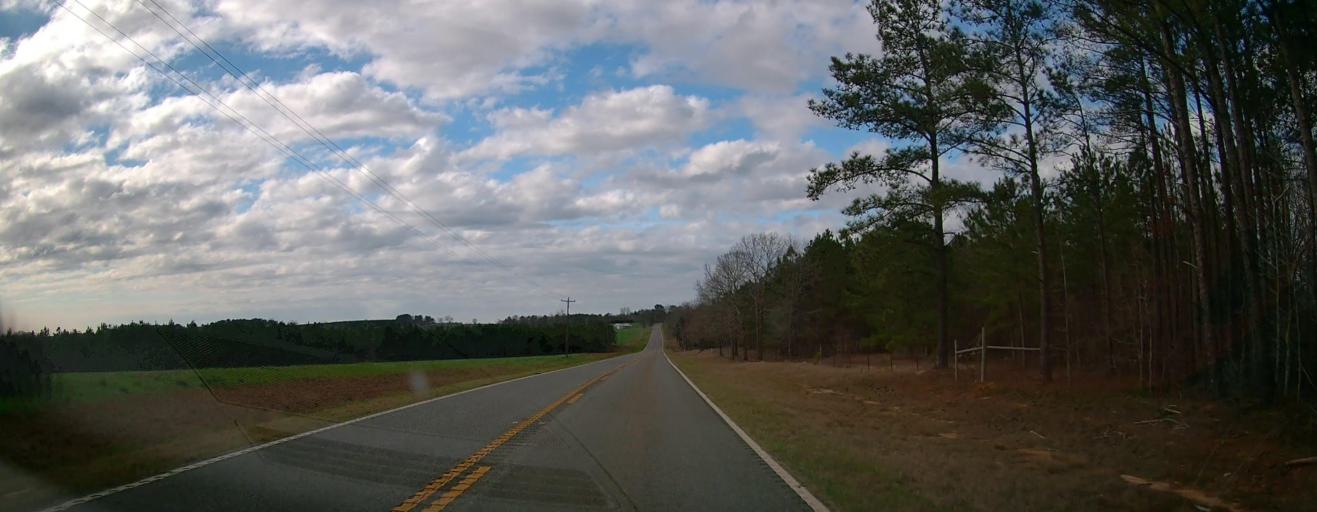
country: US
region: Georgia
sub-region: Marion County
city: Buena Vista
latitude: 32.4368
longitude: -84.4334
